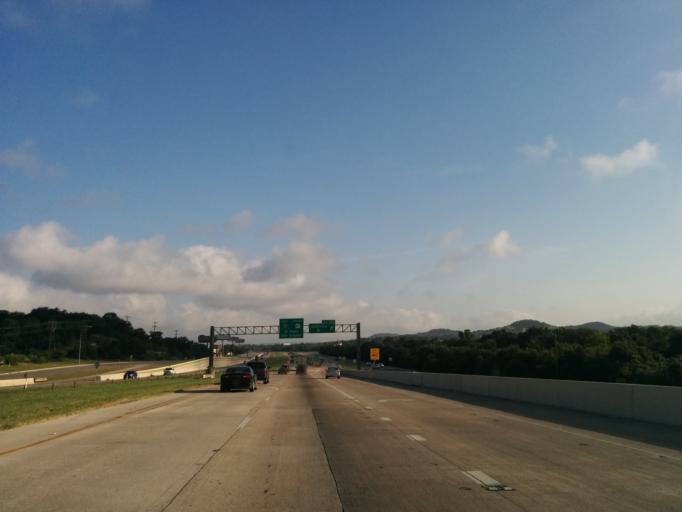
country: US
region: Texas
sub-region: Bexar County
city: Cross Mountain
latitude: 29.6264
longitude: -98.6102
